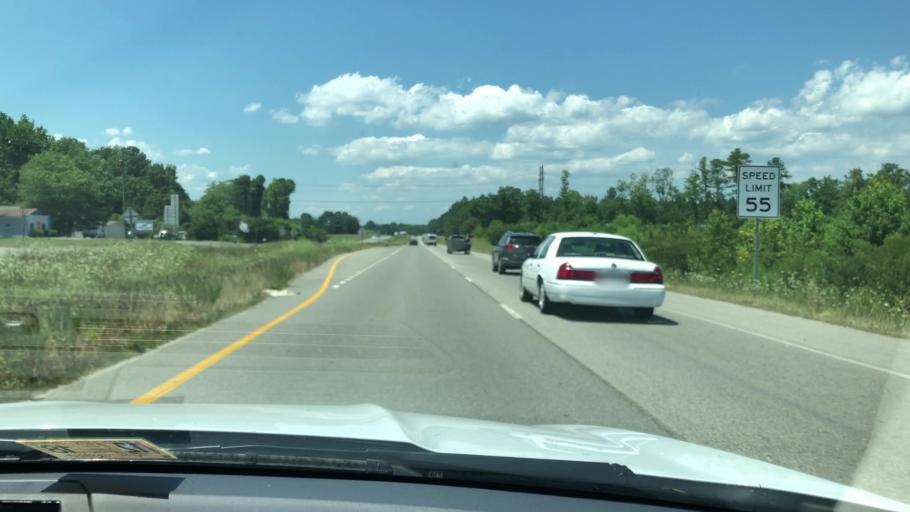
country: US
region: Virginia
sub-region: Middlesex County
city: Saluda
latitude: 37.5827
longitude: -76.4881
